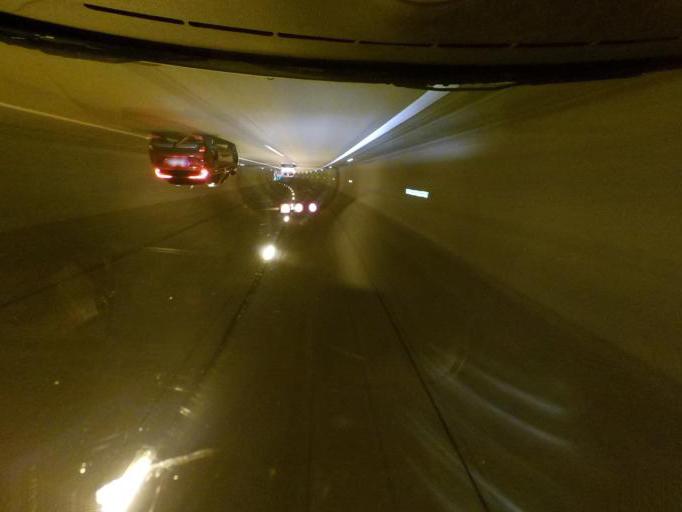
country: DE
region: Saxony
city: Bannewitz
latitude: 51.0197
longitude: 13.6967
